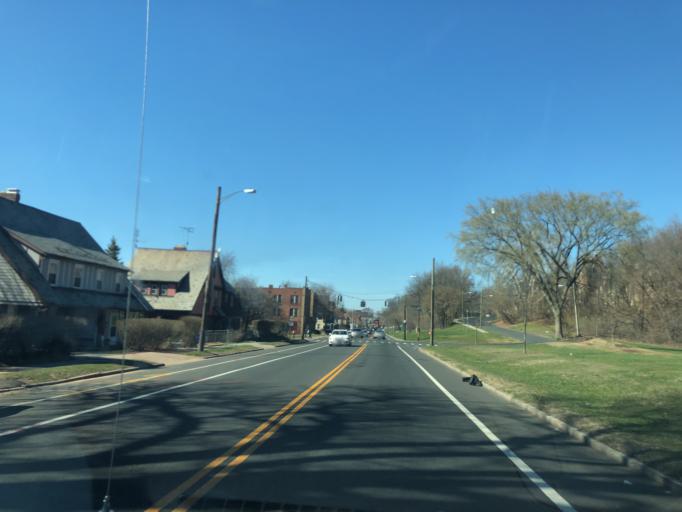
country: US
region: Connecticut
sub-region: Hartford County
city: Hartford
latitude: 41.7456
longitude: -72.6940
